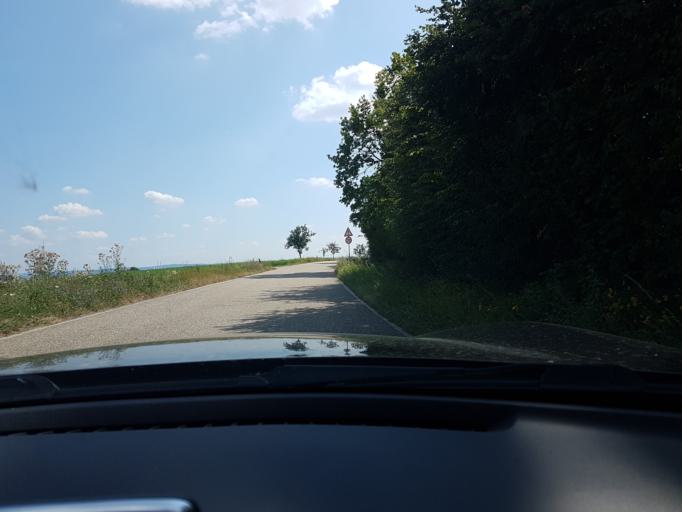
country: DE
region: Baden-Wuerttemberg
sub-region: Regierungsbezirk Stuttgart
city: Gundelsheim
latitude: 49.2656
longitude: 9.1369
